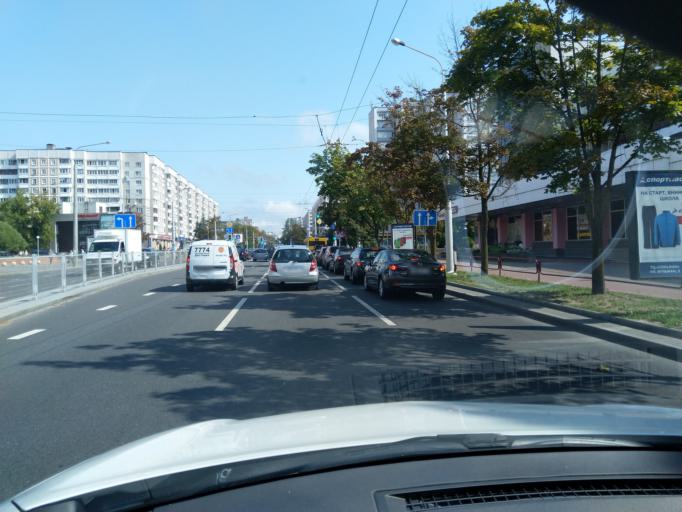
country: BY
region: Minsk
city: Minsk
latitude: 53.9213
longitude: 27.5775
